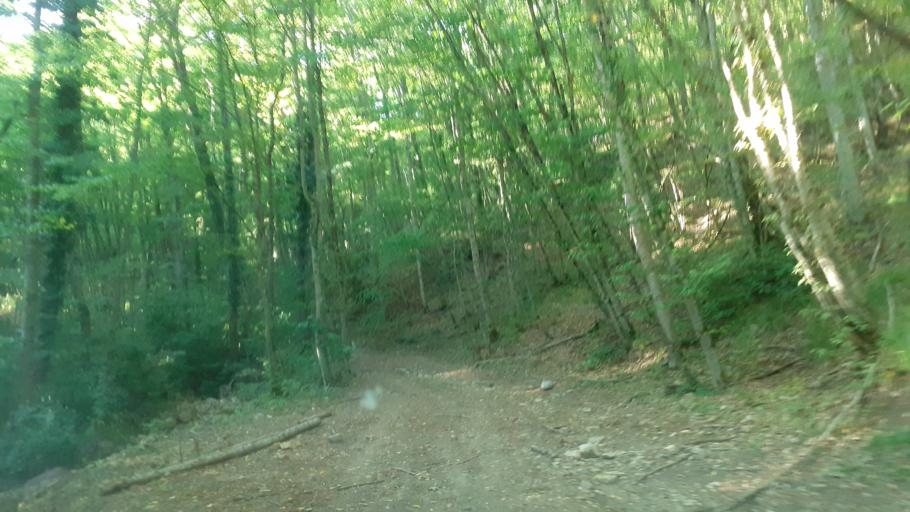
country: RU
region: Krasnodarskiy
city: Azovskaya
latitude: 44.6641
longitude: 38.4897
